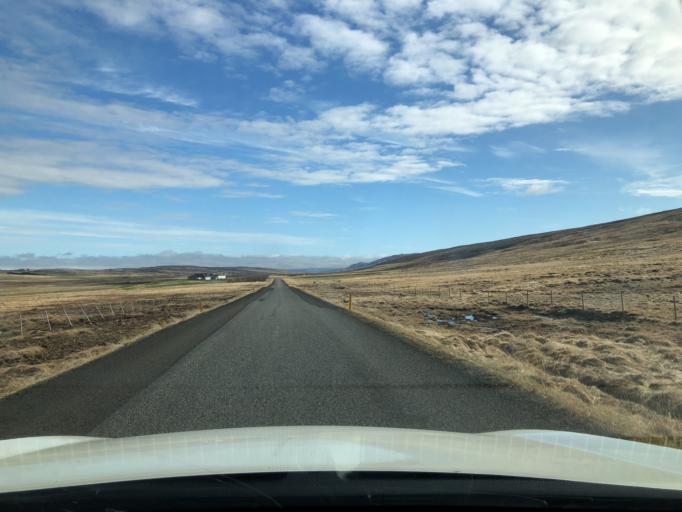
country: IS
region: West
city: Borgarnes
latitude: 65.0920
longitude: -21.7304
